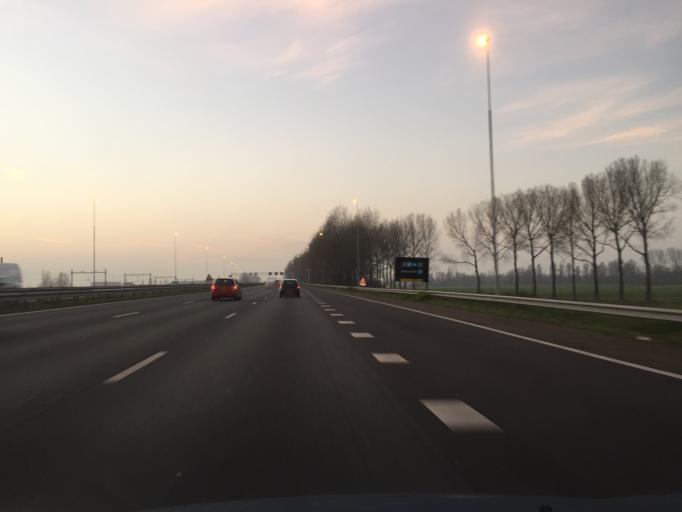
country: NL
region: South Holland
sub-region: Gemeente Pijnacker-Nootdorp
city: Pijnacker
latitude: 52.0515
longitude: 4.4294
